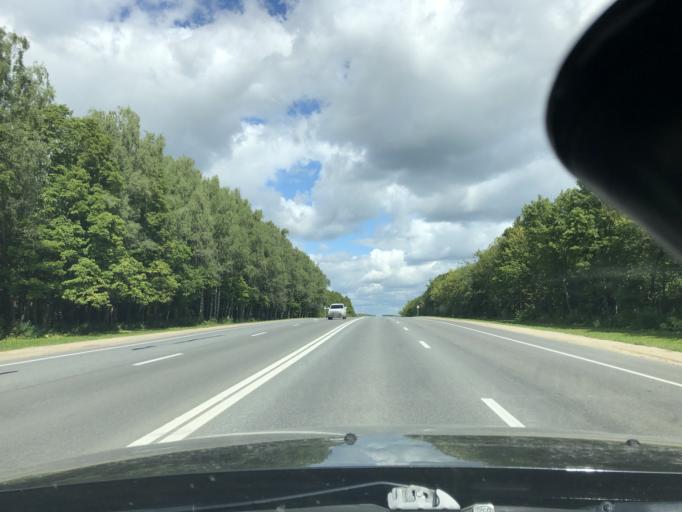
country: RU
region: Tula
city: Gorelki
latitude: 54.3133
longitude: 37.5654
